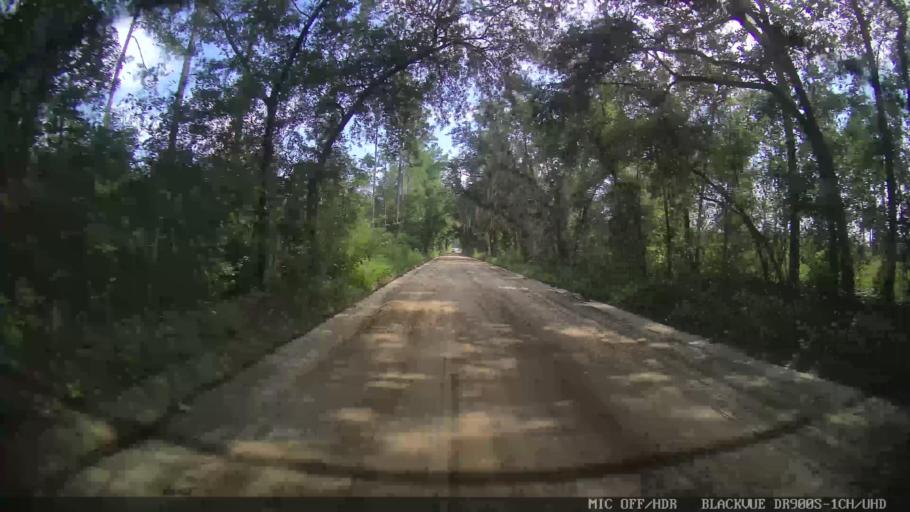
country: US
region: Georgia
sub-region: Echols County
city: Statenville
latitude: 30.6211
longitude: -83.2006
